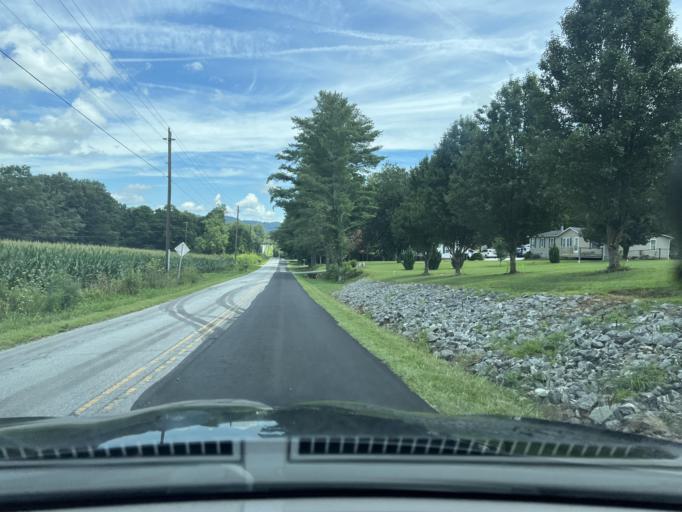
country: US
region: North Carolina
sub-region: Henderson County
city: Fruitland
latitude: 35.3928
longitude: -82.3792
